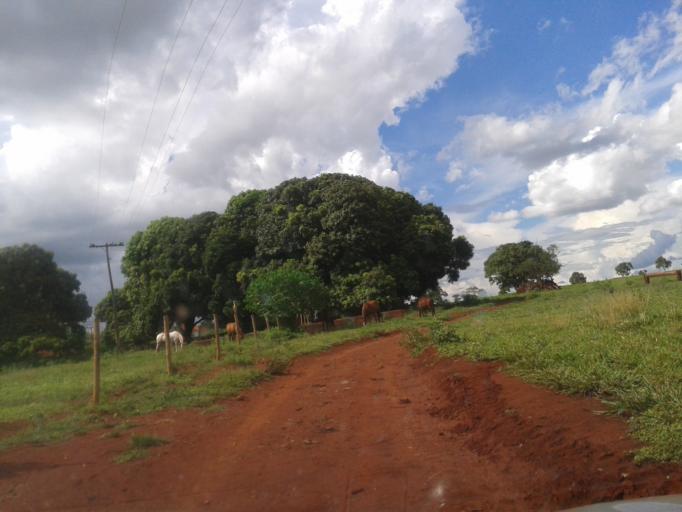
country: BR
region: Minas Gerais
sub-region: Capinopolis
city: Capinopolis
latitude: -18.7650
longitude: -49.8251
